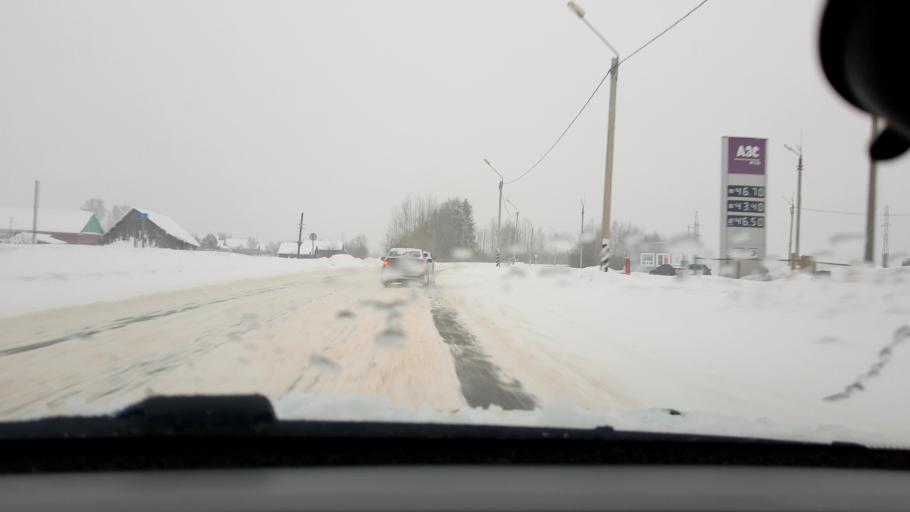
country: RU
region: Nizjnij Novgorod
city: Purekh
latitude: 56.6669
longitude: 43.1049
